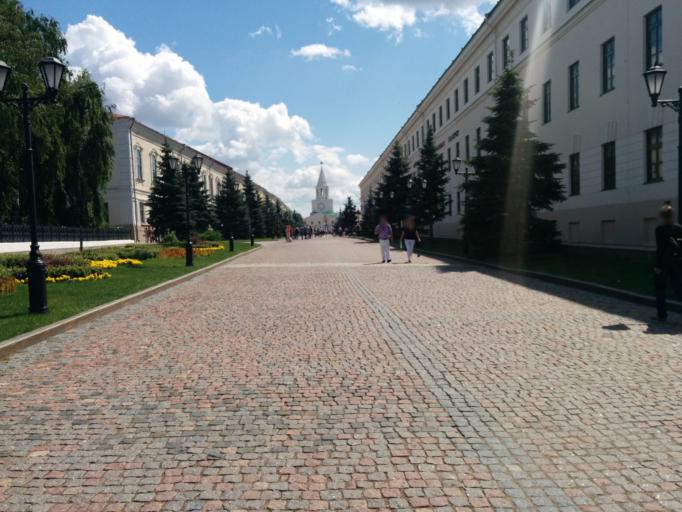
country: RU
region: Tatarstan
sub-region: Gorod Kazan'
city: Kazan
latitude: 55.7994
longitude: 49.1056
